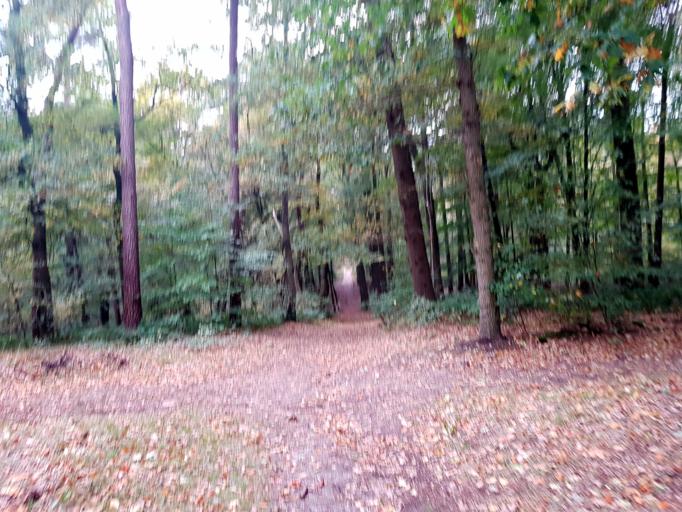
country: NL
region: Utrecht
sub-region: Gemeente Utrechtse Heuvelrug
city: Leersum
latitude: 52.0260
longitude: 5.4001
